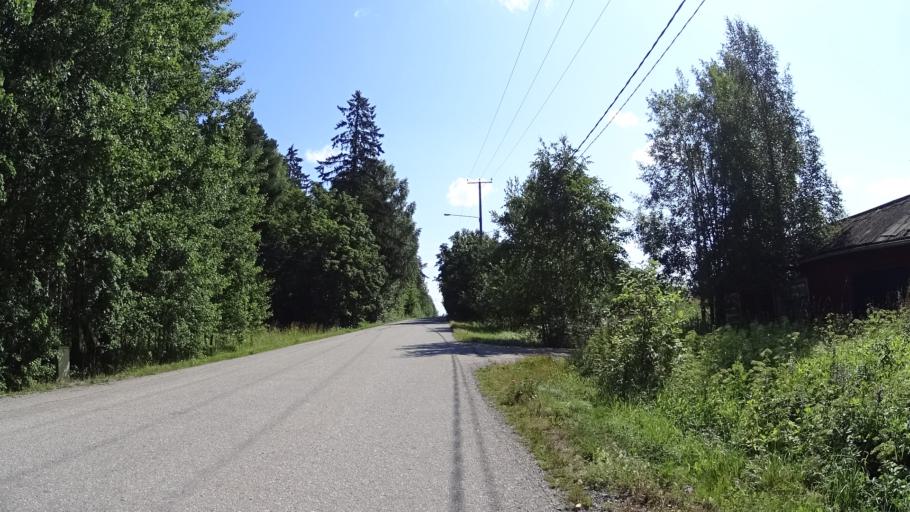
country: FI
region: Uusimaa
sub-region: Helsinki
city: Jaervenpaeae
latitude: 60.4469
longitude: 25.0860
